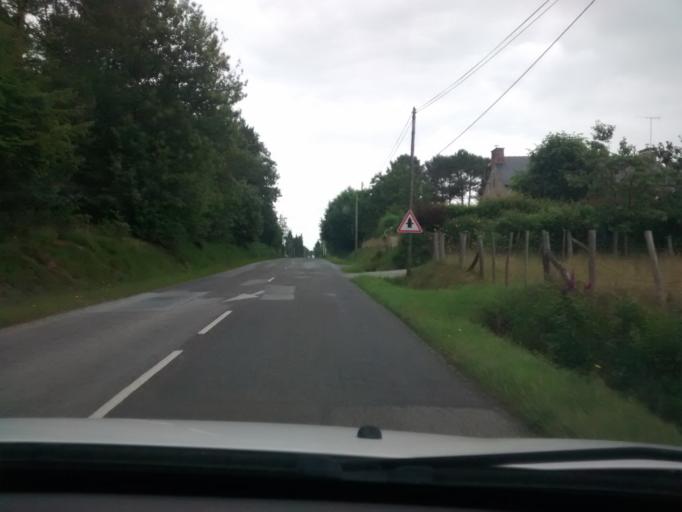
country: FR
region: Brittany
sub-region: Departement d'Ille-et-Vilaine
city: La Bouexiere
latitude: 48.1632
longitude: -1.4397
